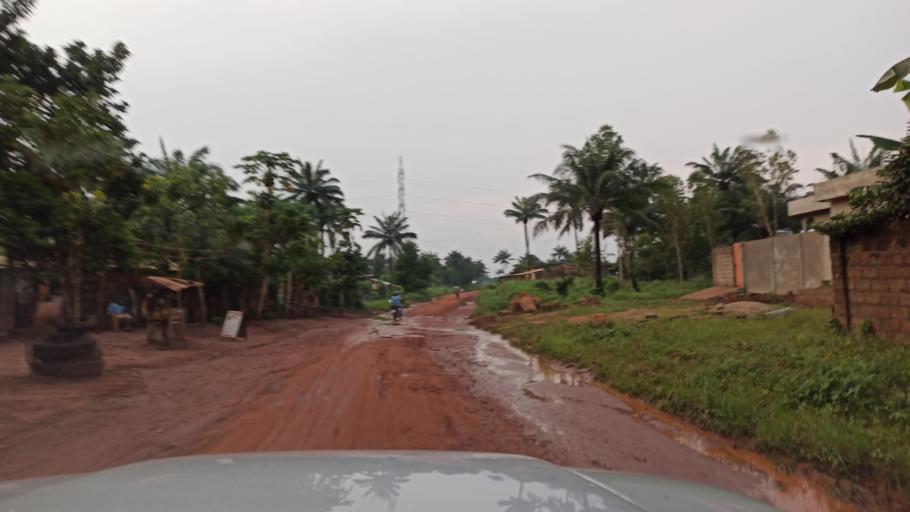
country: BJ
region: Queme
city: Porto-Novo
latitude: 6.5415
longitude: 2.6220
